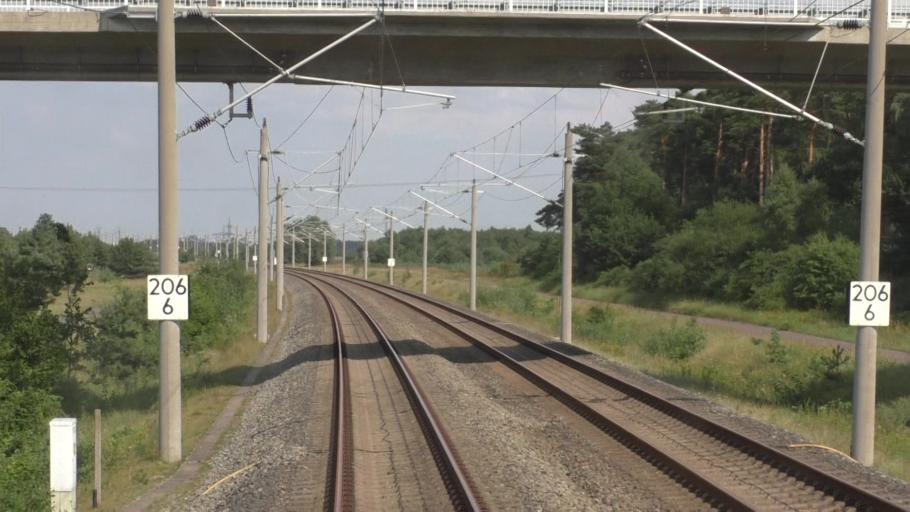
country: DE
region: Saxony-Anhalt
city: Stendal
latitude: 52.5725
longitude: 11.8410
